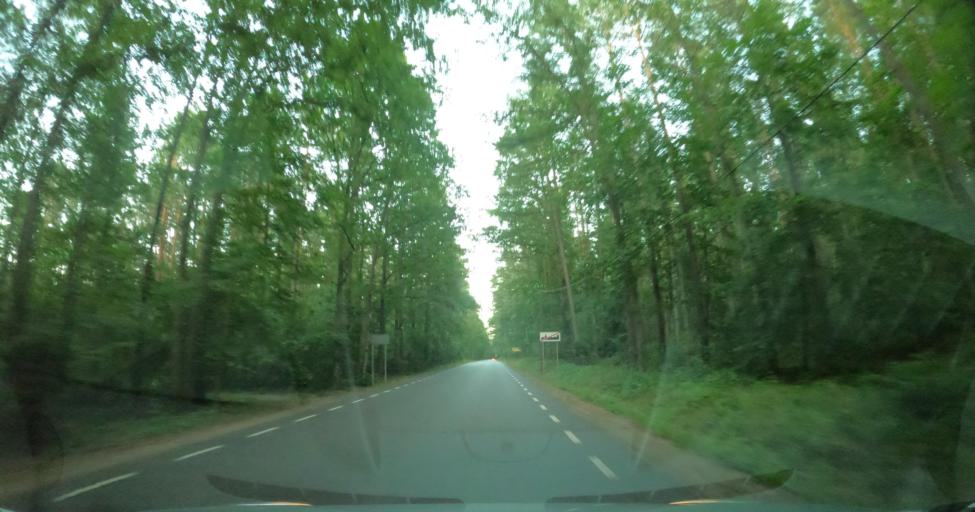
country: PL
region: Pomeranian Voivodeship
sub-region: Powiat leborski
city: Lebork
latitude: 54.5217
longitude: 17.7814
